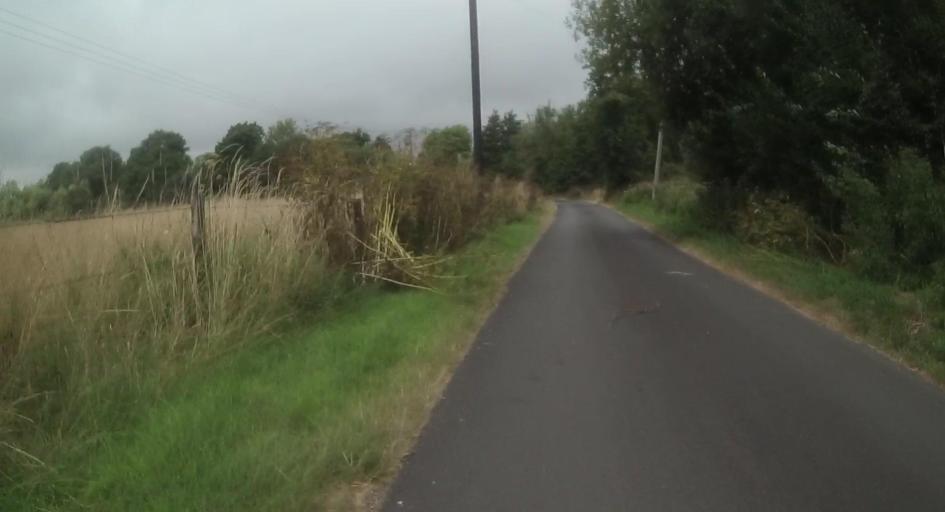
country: GB
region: England
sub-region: Dorset
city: Wool
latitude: 50.7158
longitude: -2.1930
